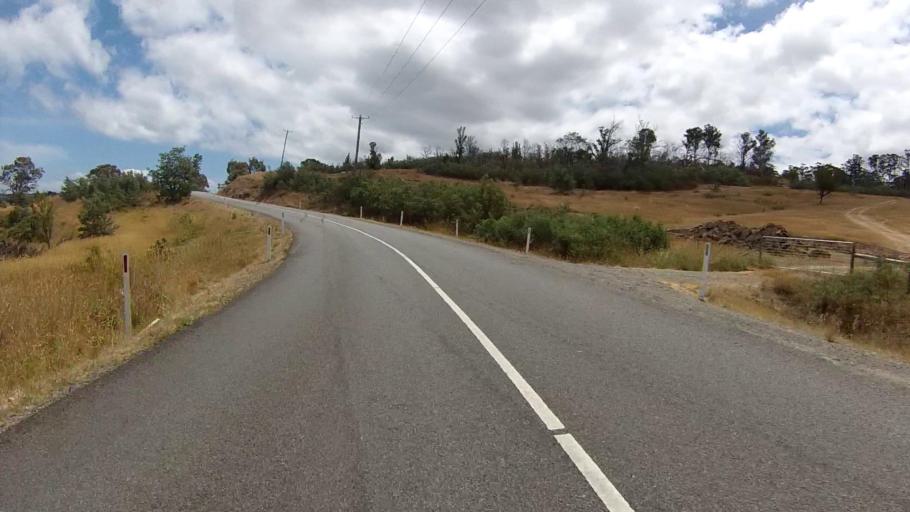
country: AU
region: Tasmania
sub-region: Sorell
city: Sorell
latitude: -42.8634
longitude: 147.6901
